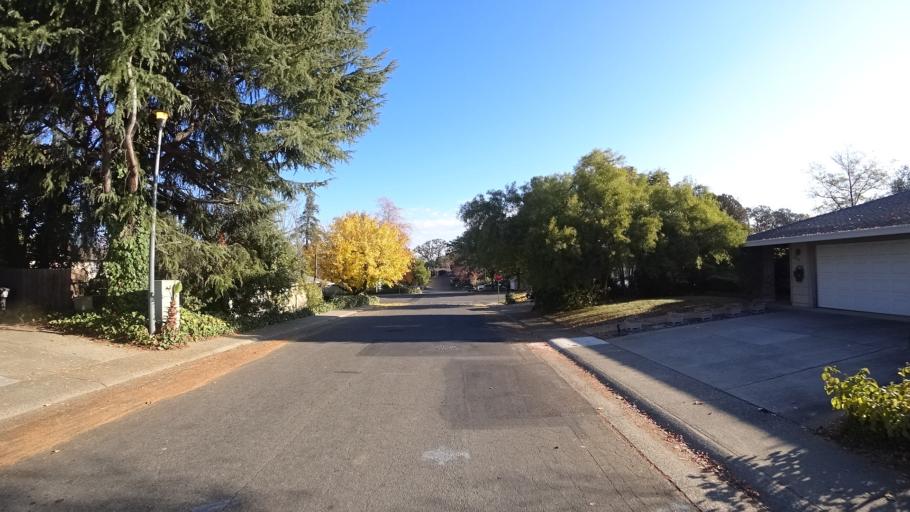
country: US
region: California
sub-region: Sacramento County
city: Citrus Heights
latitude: 38.7119
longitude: -121.2552
